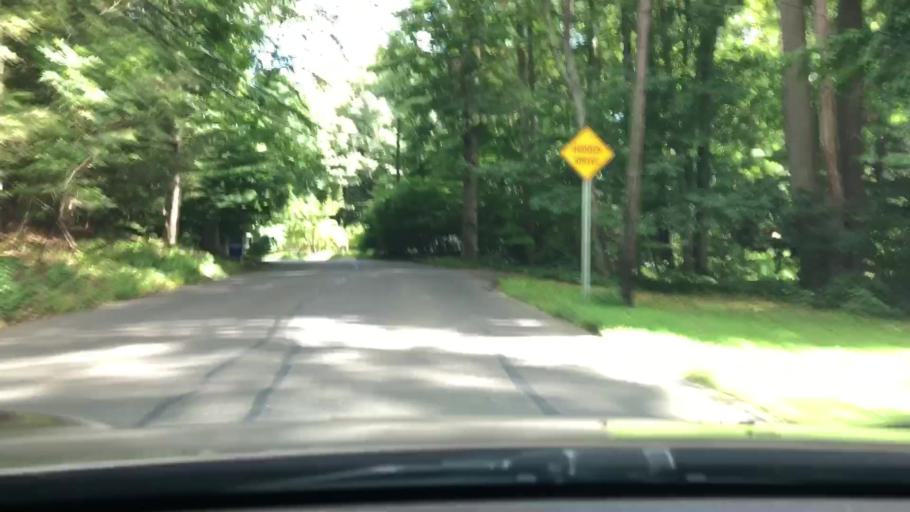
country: US
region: Connecticut
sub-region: Fairfield County
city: Darien
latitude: 41.1101
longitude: -73.4586
